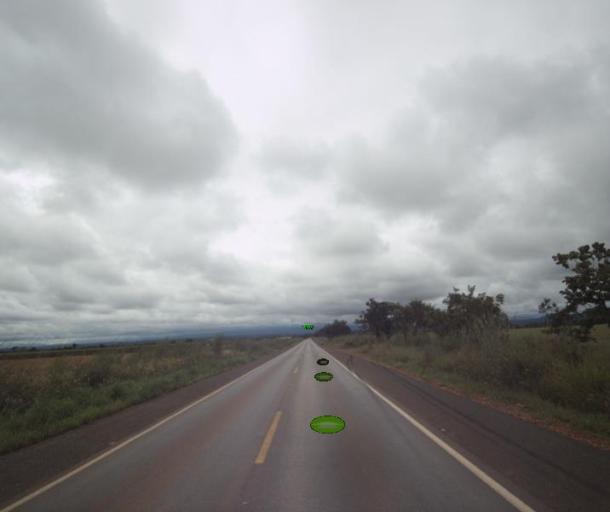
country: BR
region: Goias
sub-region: Uruacu
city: Uruacu
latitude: -14.7120
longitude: -49.0924
